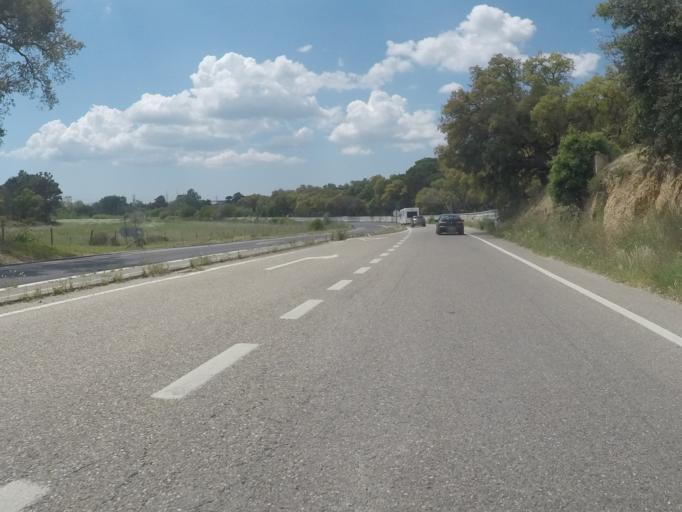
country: PT
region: Setubal
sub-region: Setubal
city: Setubal
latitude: 38.5443
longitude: -8.8279
